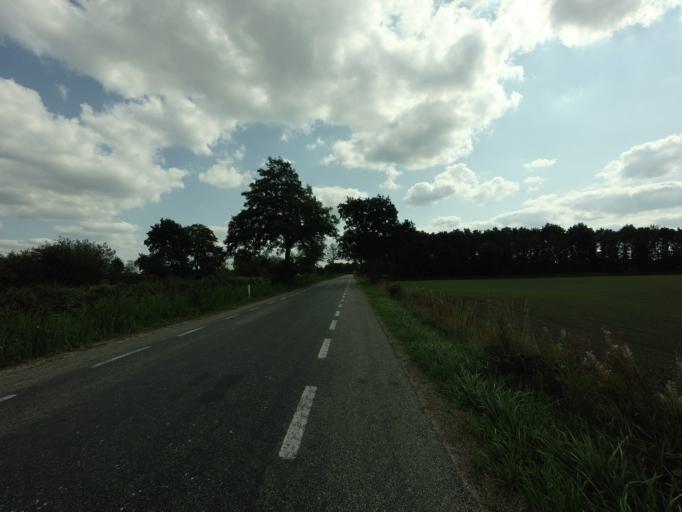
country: NL
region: Drenthe
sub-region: Gemeente Westerveld
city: Dwingeloo
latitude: 52.8752
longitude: 6.4351
